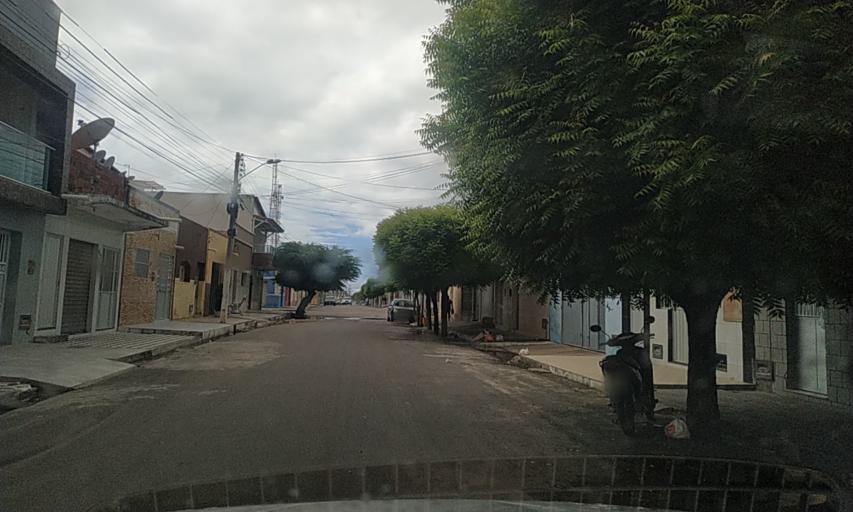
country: BR
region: Rio Grande do Norte
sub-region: Areia Branca
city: Areia Branca
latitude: -4.9558
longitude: -37.1340
